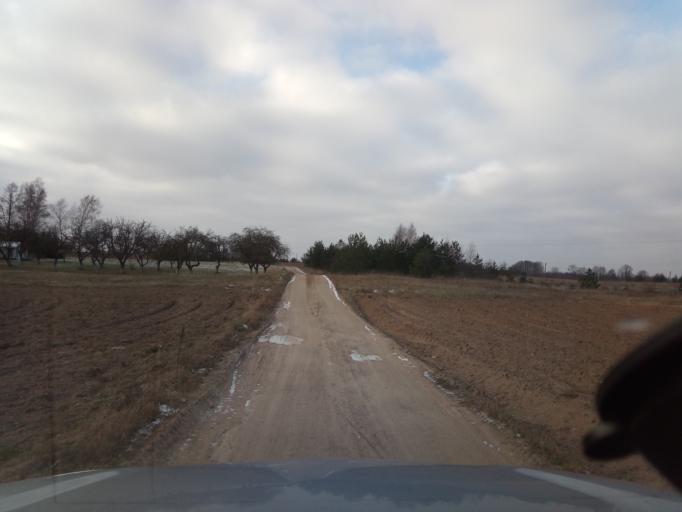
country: LT
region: Alytaus apskritis
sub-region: Alytaus rajonas
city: Daugai
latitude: 54.3736
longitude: 24.3882
